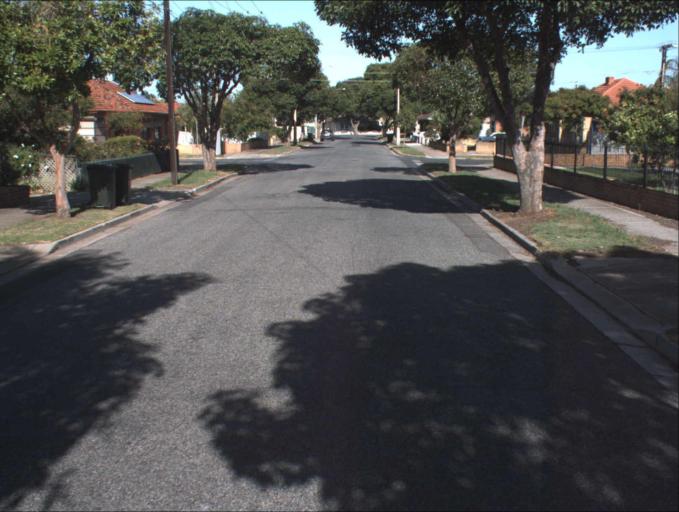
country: AU
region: South Australia
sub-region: Charles Sturt
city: Woodville
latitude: -34.8844
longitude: 138.5686
